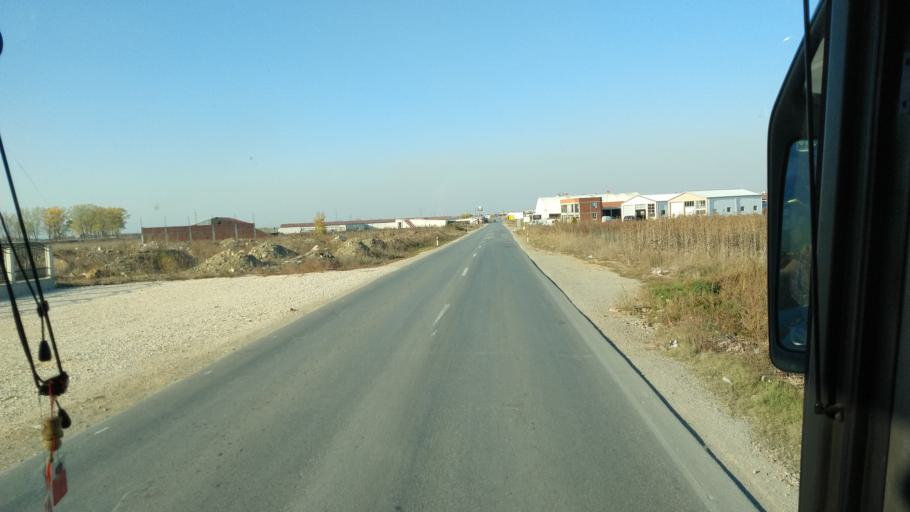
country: XK
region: Pristina
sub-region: Lipjan
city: Lipljan
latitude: 42.5166
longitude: 21.1126
